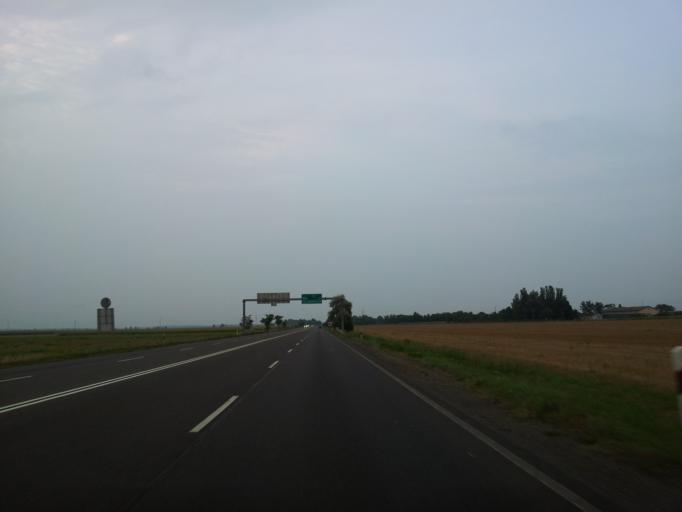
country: HU
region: Tolna
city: Szekszard
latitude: 46.3921
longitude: 18.7136
